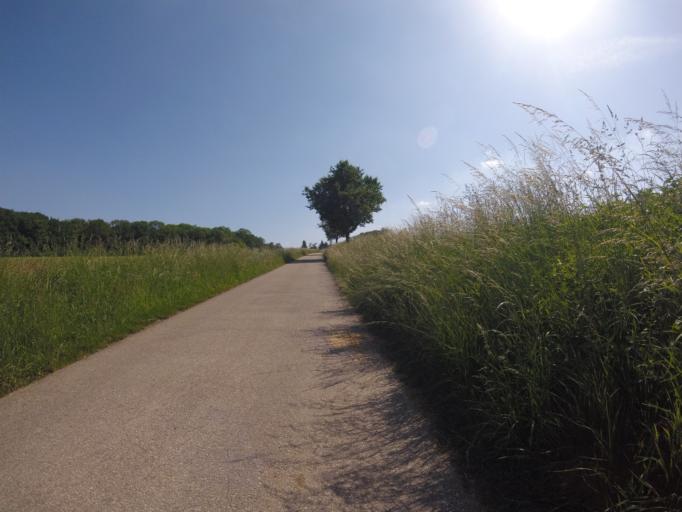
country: DE
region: Baden-Wuerttemberg
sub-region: Regierungsbezirk Stuttgart
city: Kirchberg an der Murr
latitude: 48.9698
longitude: 9.3275
